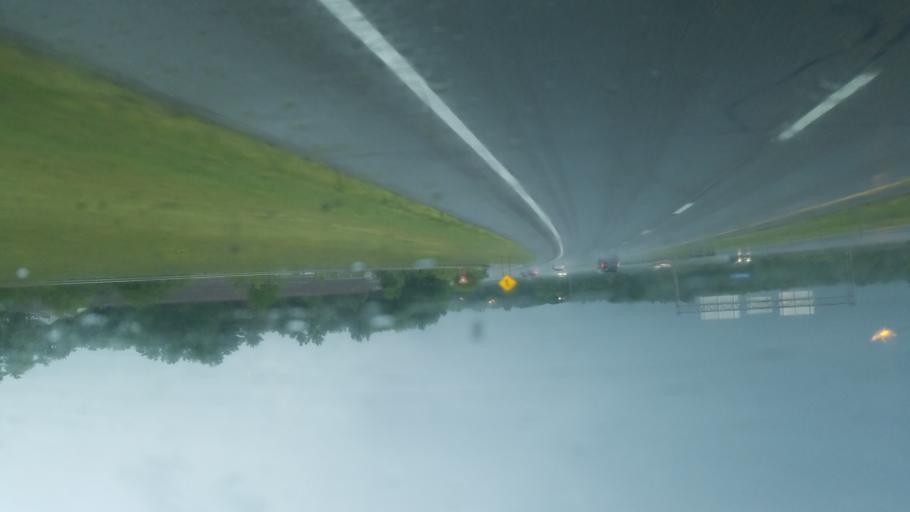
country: US
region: Ohio
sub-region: Trumbull County
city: Morgandale
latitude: 41.2735
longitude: -80.7759
